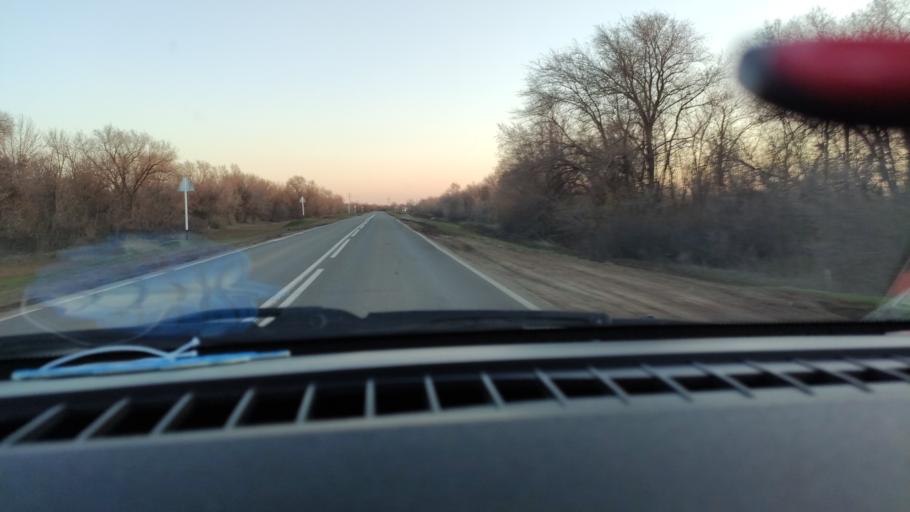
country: RU
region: Saratov
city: Privolzhskiy
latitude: 51.3262
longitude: 46.0316
